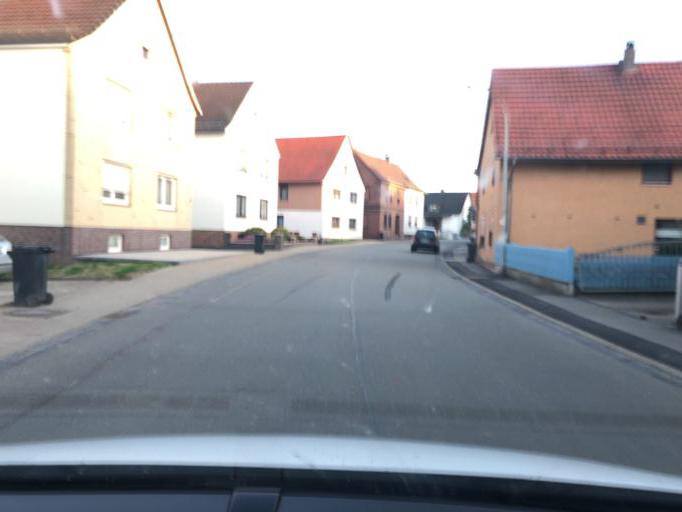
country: DE
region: Thuringia
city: Brehme
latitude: 51.5502
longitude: 10.3601
